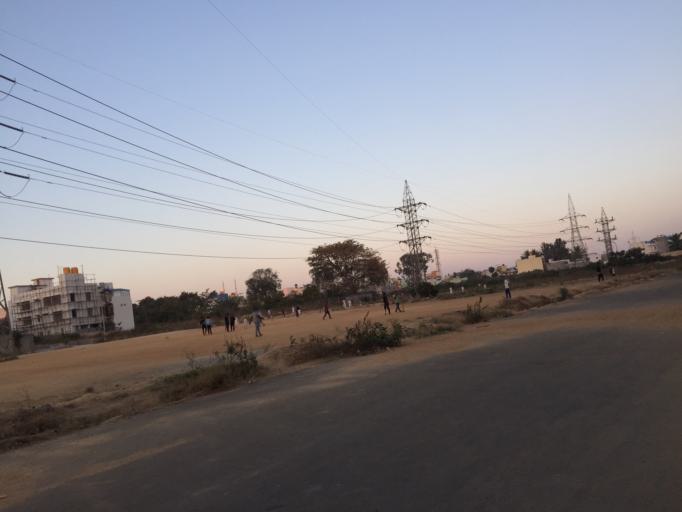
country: IN
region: Karnataka
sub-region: Bangalore Urban
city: Yelahanka
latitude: 13.0508
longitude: 77.6232
